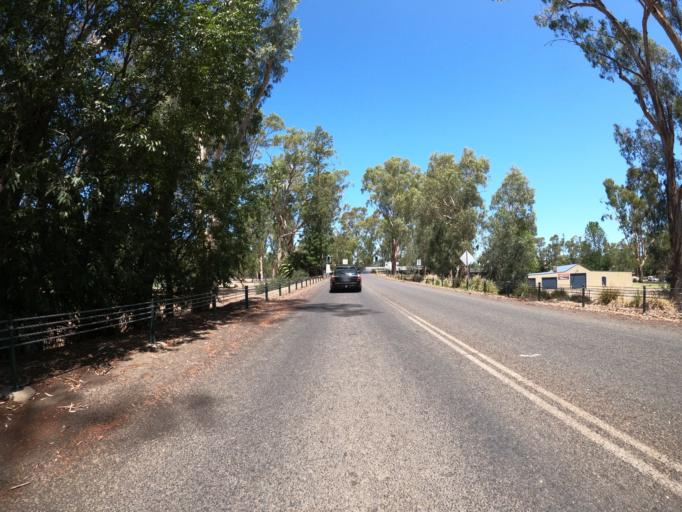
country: AU
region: New South Wales
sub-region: Corowa Shire
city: Corowa
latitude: -36.0052
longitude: 146.3950
